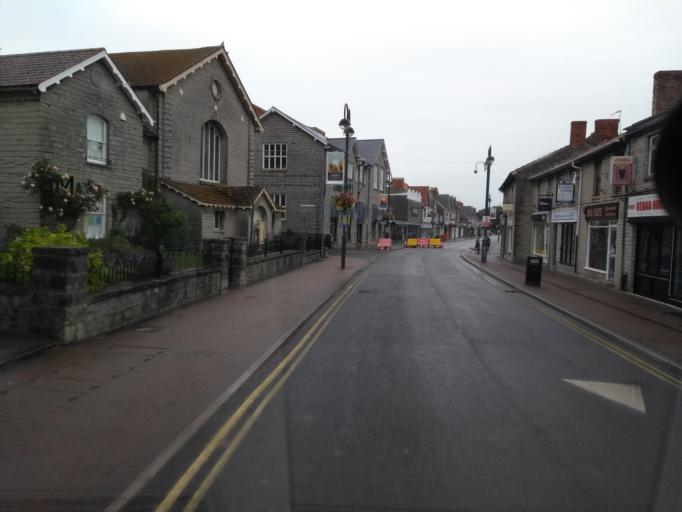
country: GB
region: England
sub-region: Somerset
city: Street
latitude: 51.1254
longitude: -2.7427
